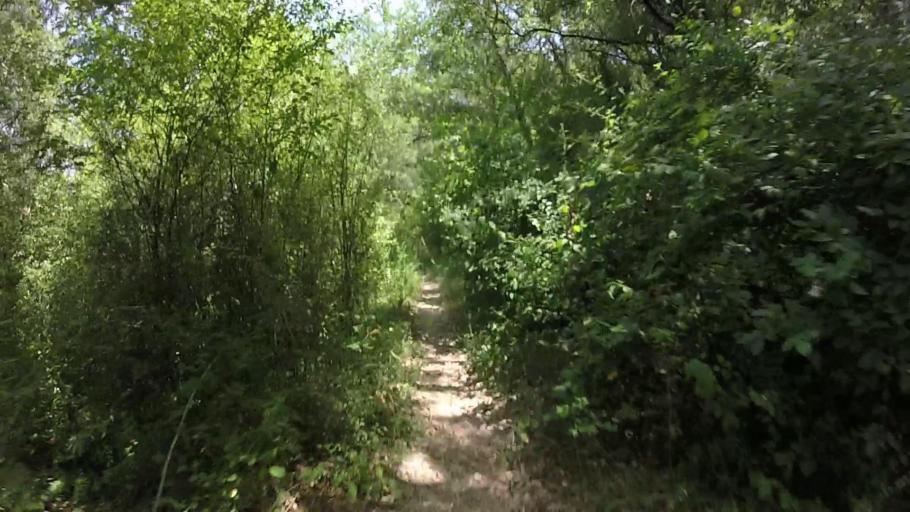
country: FR
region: Provence-Alpes-Cote d'Azur
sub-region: Departement des Alpes-Maritimes
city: Mougins
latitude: 43.6178
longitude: 7.0171
